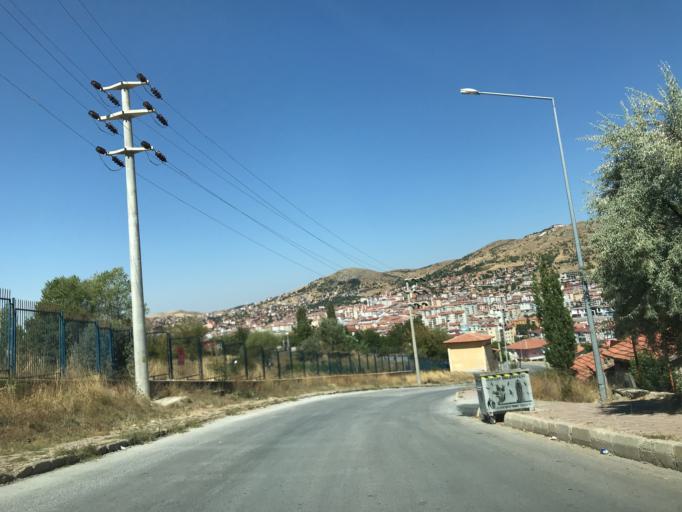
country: TR
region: Yozgat
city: Yozgat
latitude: 39.8171
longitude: 34.8198
